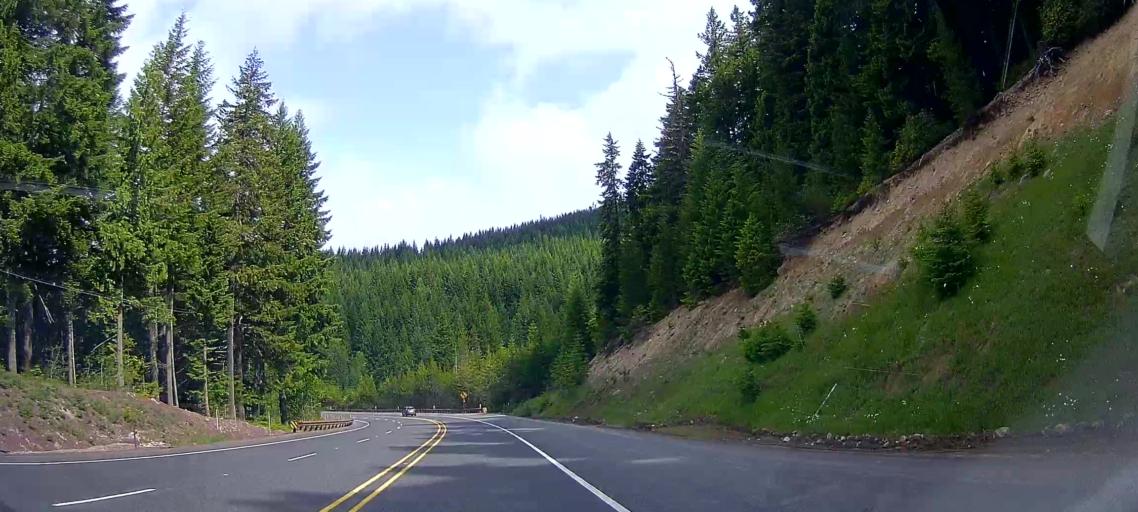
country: US
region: Oregon
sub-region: Clackamas County
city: Mount Hood Village
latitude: 45.2397
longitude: -121.6992
